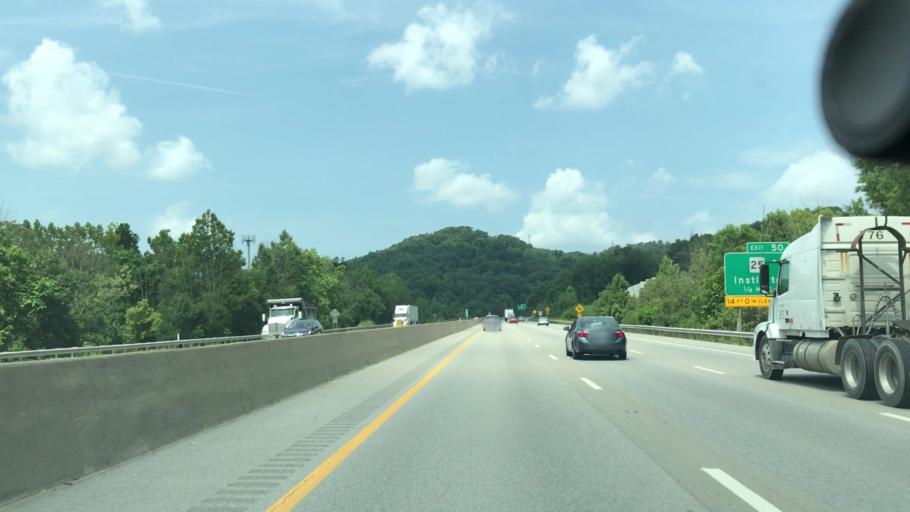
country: US
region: West Virginia
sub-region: Kanawha County
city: Dunbar
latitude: 38.3841
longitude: -81.7636
